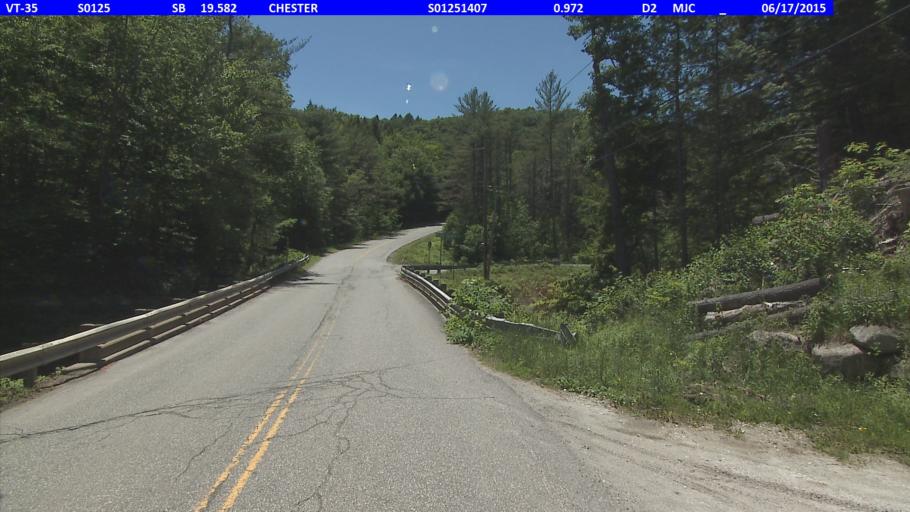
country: US
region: Vermont
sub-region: Windsor County
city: Chester
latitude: 43.2432
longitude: -72.6071
